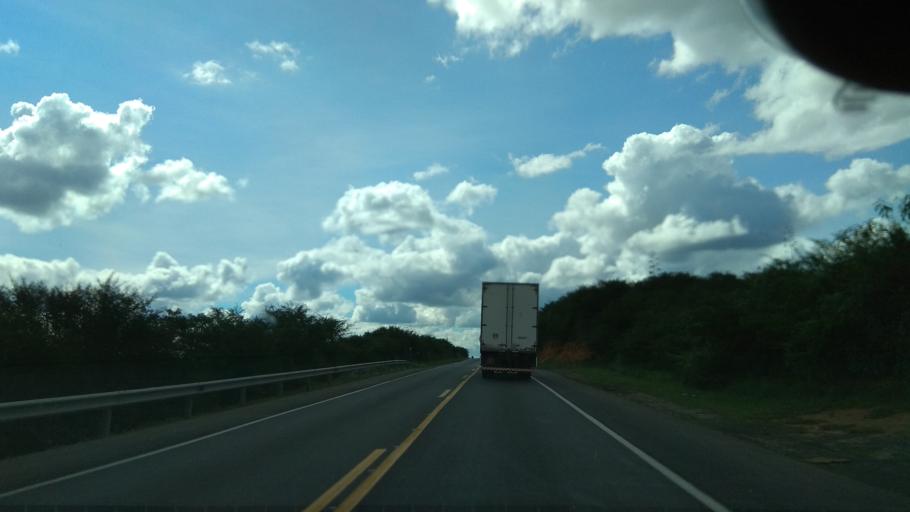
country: BR
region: Bahia
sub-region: Jaguaquara
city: Jaguaquara
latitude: -13.4449
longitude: -40.0307
